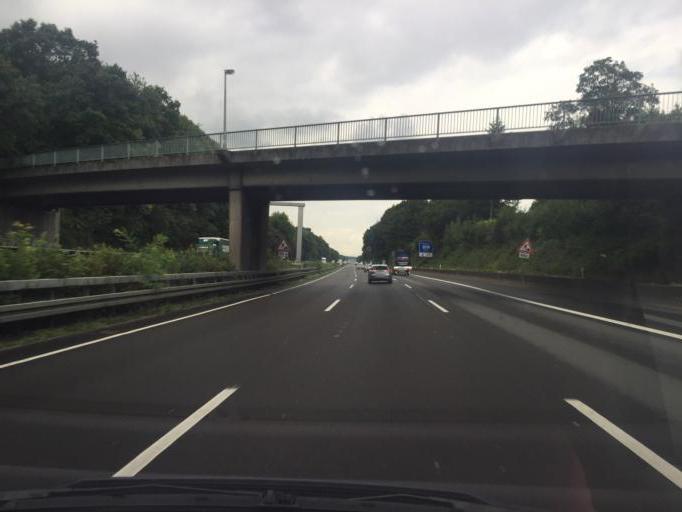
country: DE
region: North Rhine-Westphalia
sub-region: Regierungsbezirk Koln
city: Rosrath
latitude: 50.8951
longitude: 7.1655
